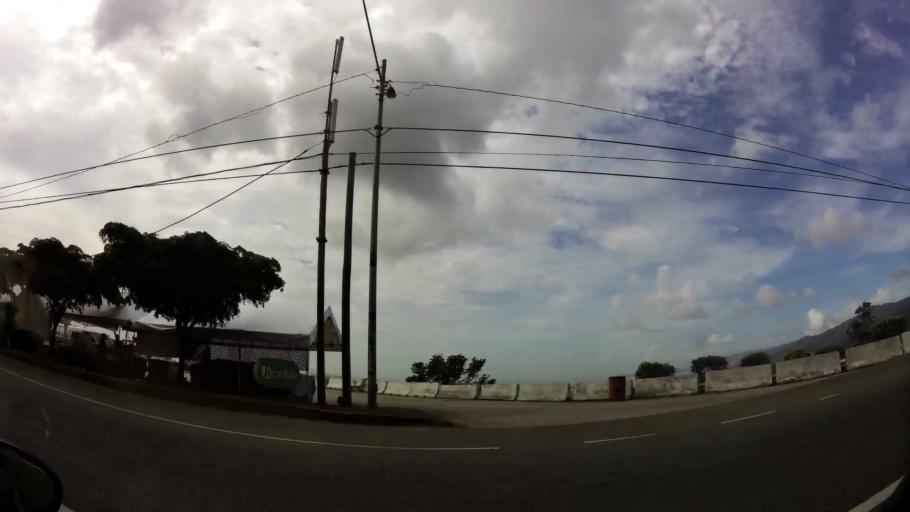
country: TT
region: San Juan/Laventille
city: Laventille
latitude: 10.6703
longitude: -61.4912
